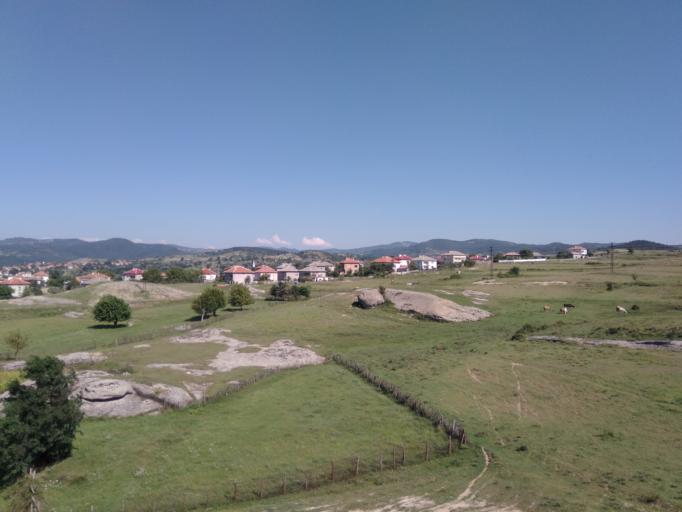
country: BG
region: Kurdzhali
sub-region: Obshtina Dzhebel
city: Dzhebel
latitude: 41.3809
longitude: 25.2627
